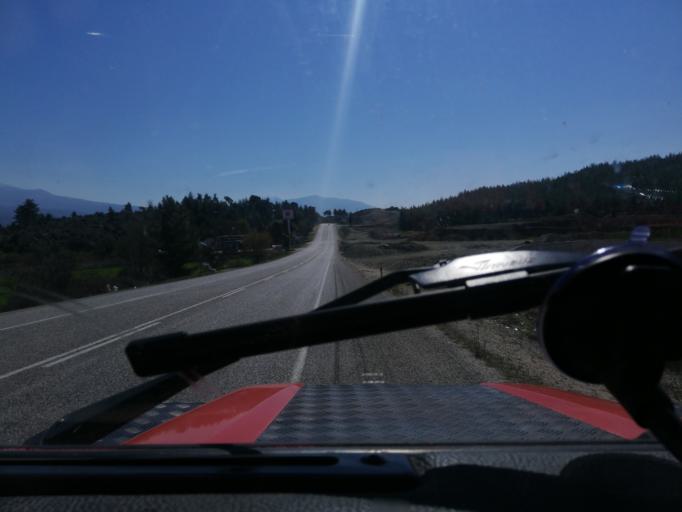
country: TR
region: Mugla
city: Kemer
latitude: 36.6151
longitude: 29.3573
